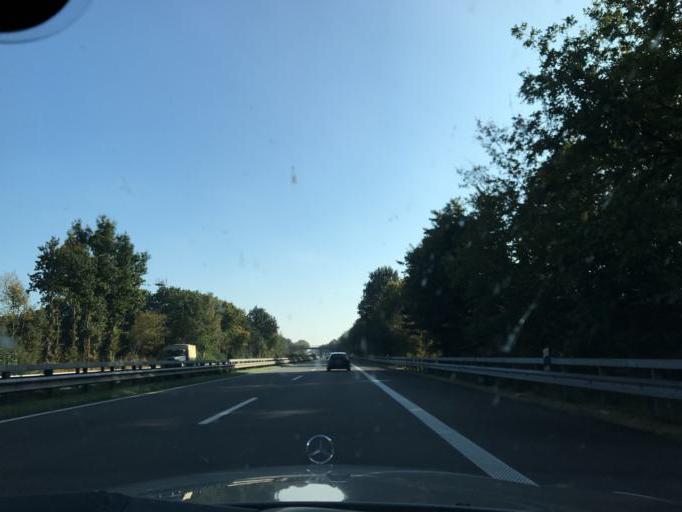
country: DE
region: Lower Saxony
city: Bad Zwischenahn
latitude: 53.2323
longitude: 8.0316
